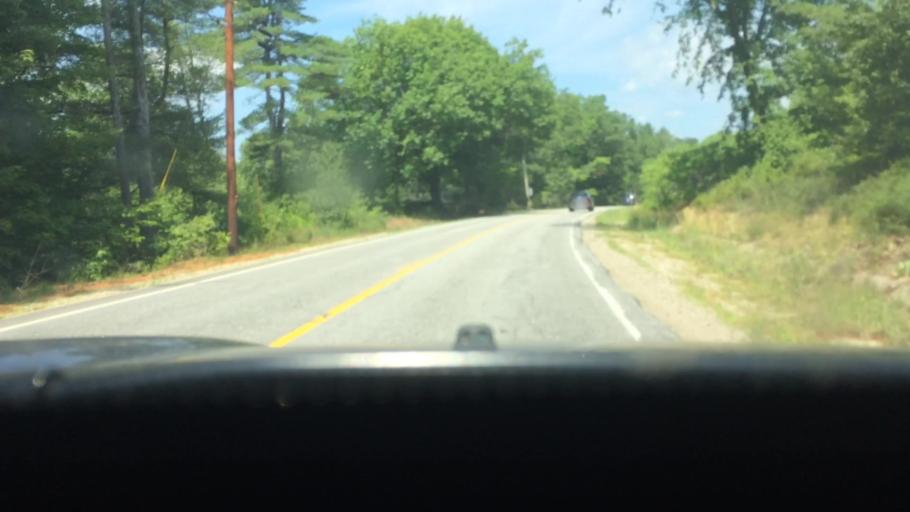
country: US
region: Maine
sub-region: Androscoggin County
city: Mechanic Falls
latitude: 44.1207
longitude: -70.4311
